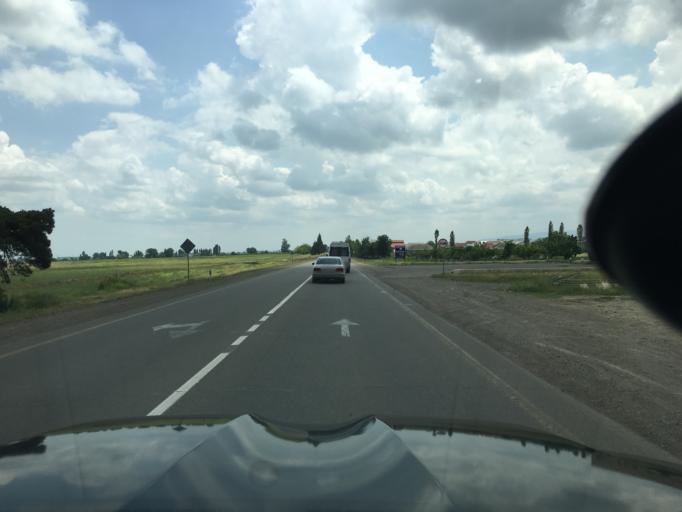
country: AZ
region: Tovuz
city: Tovuz
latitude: 40.9561
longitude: 45.7347
